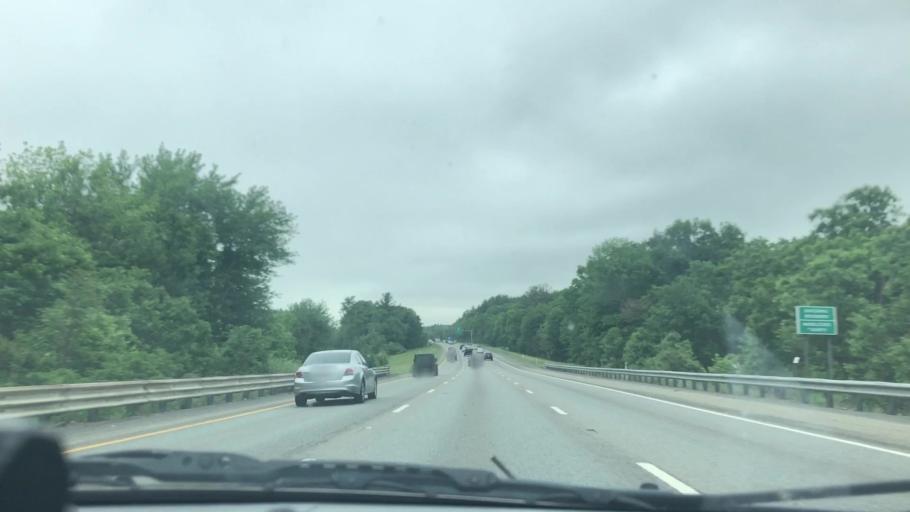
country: US
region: Massachusetts
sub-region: Worcester County
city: Harvard
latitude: 42.4722
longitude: -71.5562
